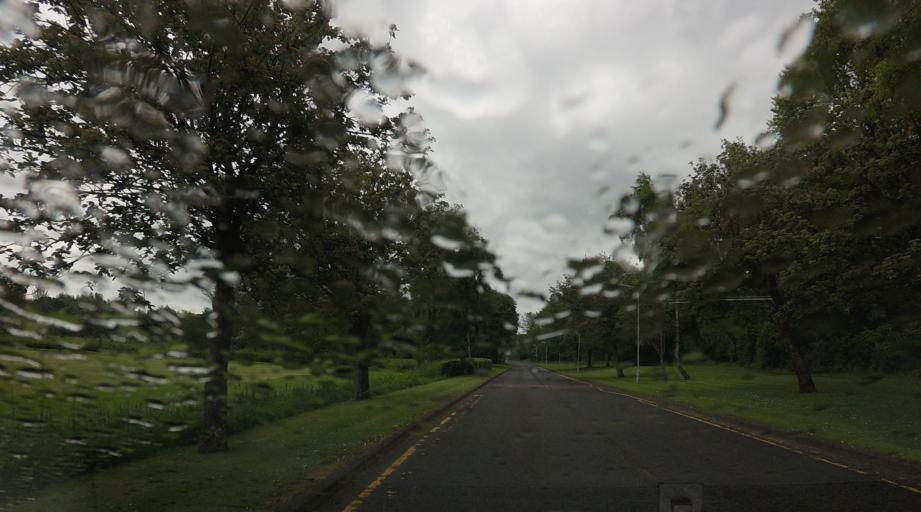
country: GB
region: Scotland
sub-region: Fife
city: Ballingry
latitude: 56.1500
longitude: -3.3345
